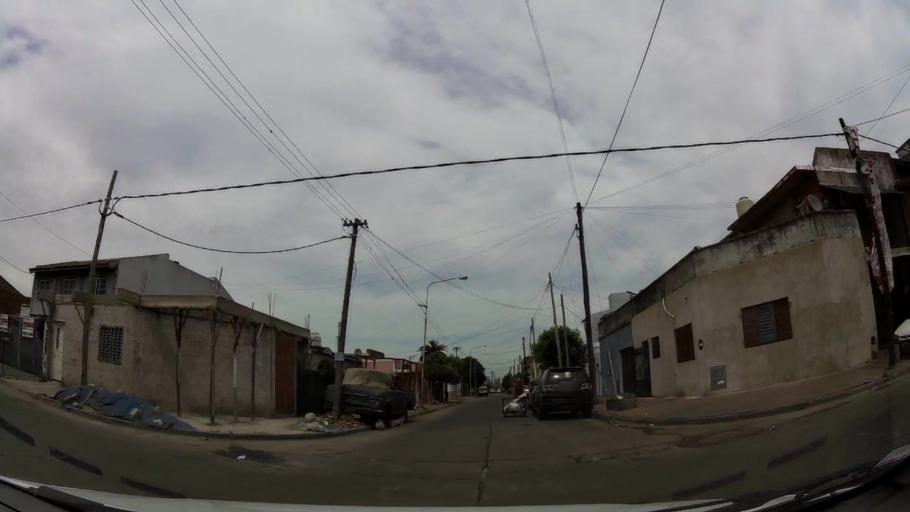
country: AR
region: Buenos Aires
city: San Justo
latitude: -34.6864
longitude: -58.5340
